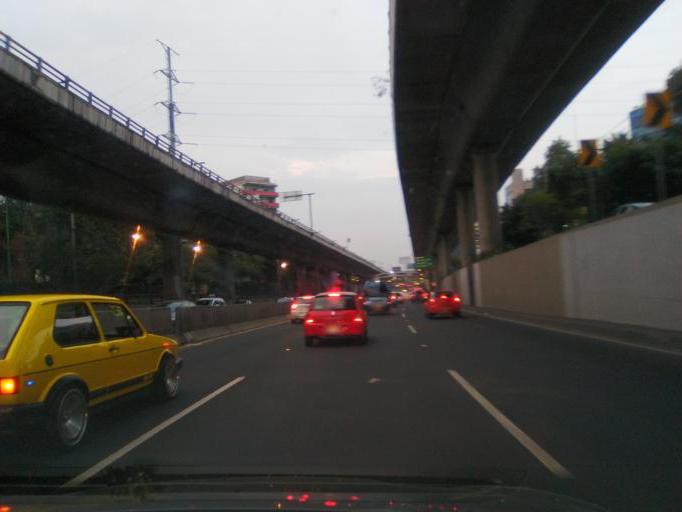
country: MX
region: Mexico City
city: Magdalena Contreras
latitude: 19.3350
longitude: -99.2079
